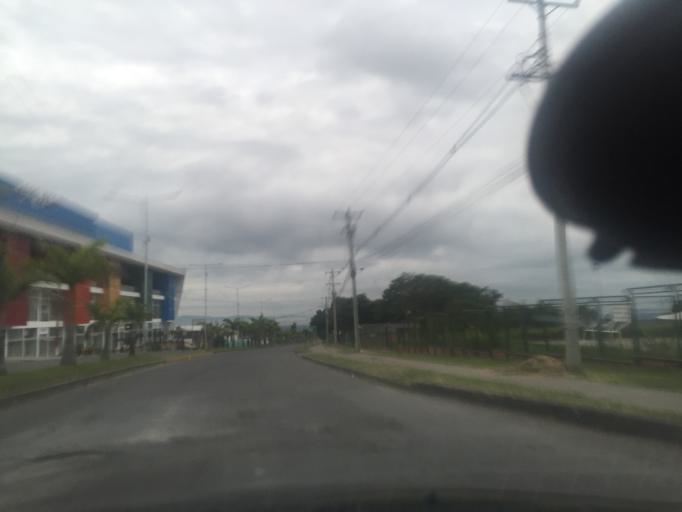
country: CO
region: Quindio
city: Armenia
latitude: 4.5150
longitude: -75.6972
